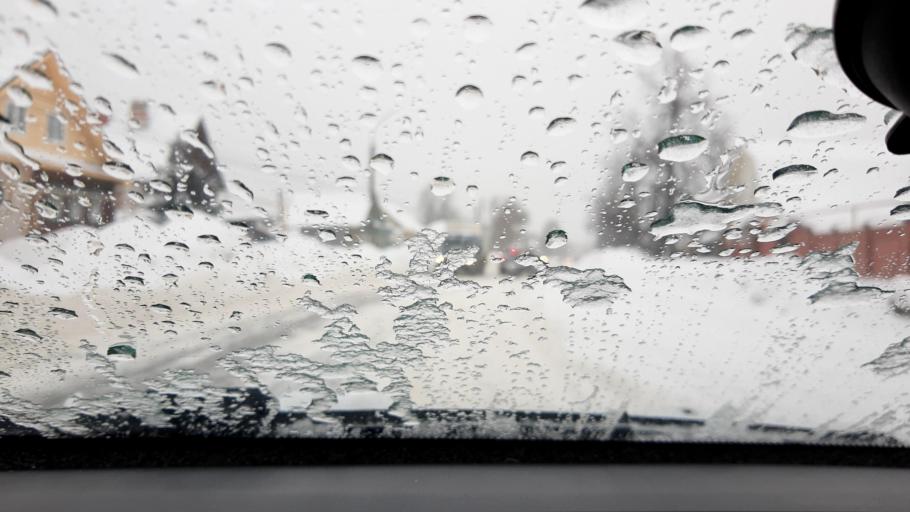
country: RU
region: Nizjnij Novgorod
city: Novaya Balakhna
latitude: 56.5158
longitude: 43.5840
